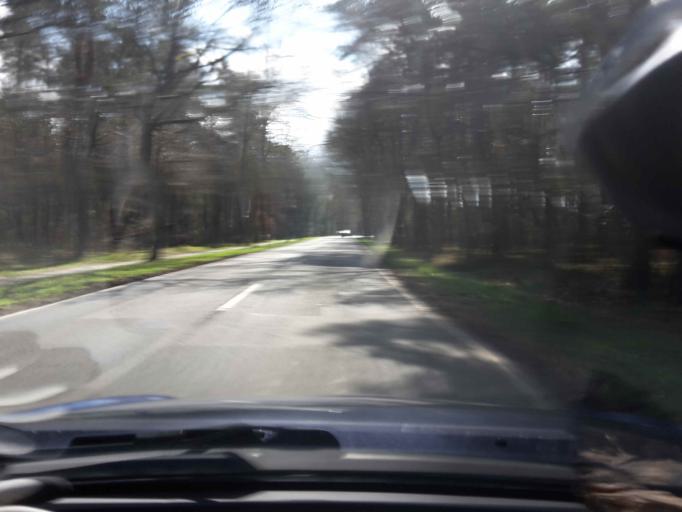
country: DE
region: Lower Saxony
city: Hanstedt
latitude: 53.2812
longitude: 10.0062
